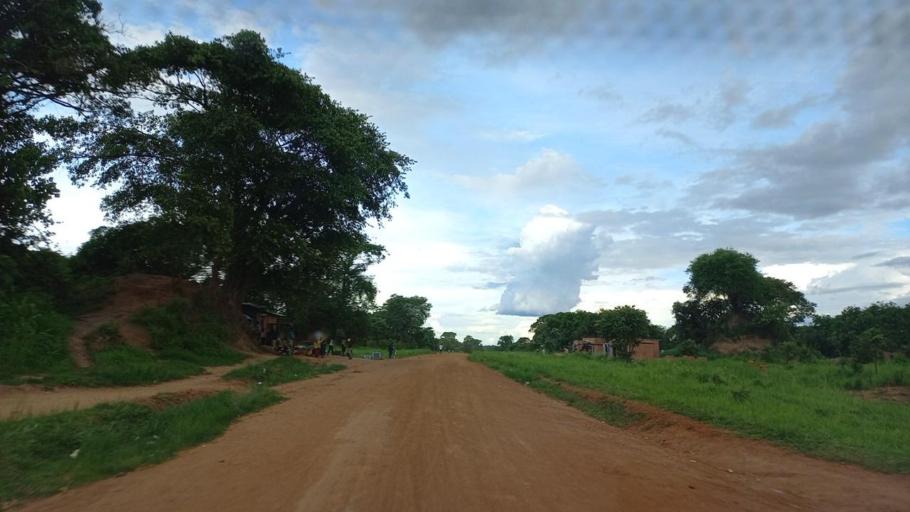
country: ZM
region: North-Western
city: Mwinilunga
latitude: -11.7585
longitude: 24.4220
